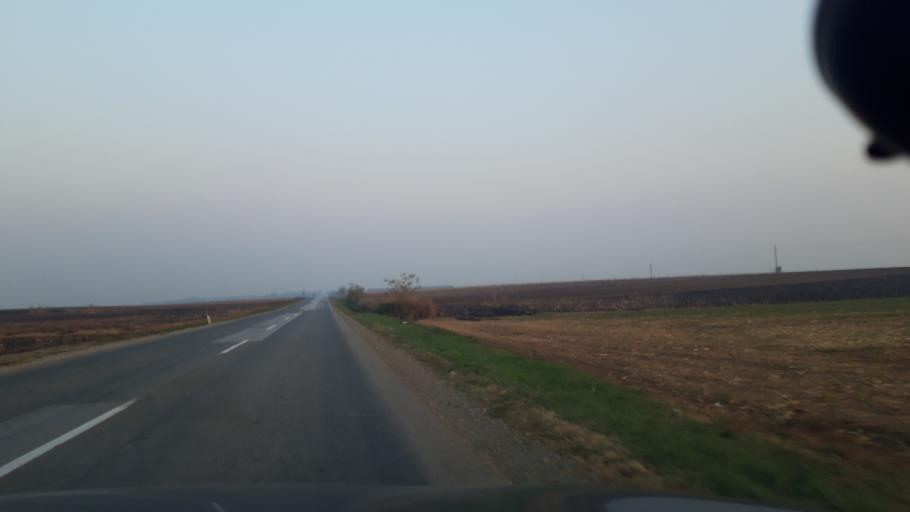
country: RS
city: Putinci
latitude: 45.0063
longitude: 19.9071
